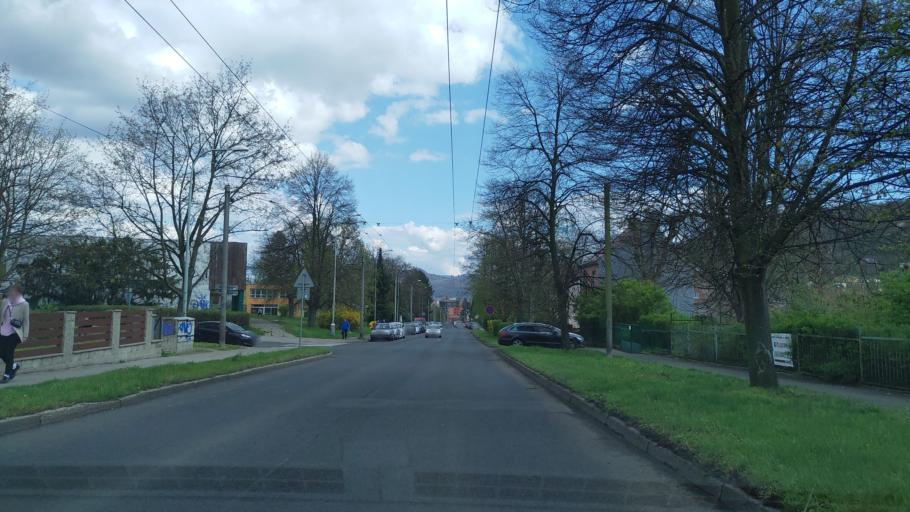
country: CZ
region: Ustecky
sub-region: Okres Usti nad Labem
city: Usti nad Labem
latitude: 50.6841
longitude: 14.0004
